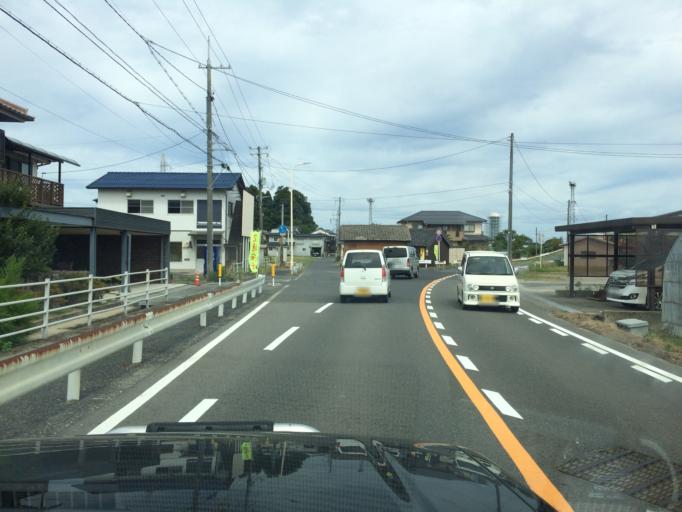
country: JP
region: Tottori
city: Tottori
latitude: 35.5073
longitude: 134.1930
